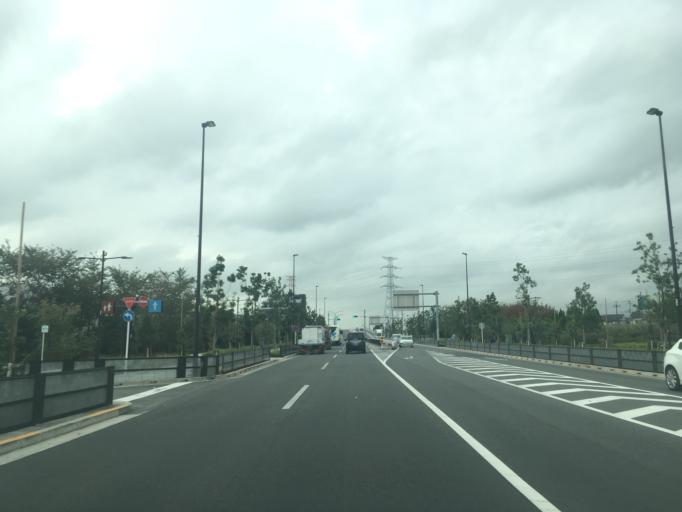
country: JP
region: Tokyo
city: Kokubunji
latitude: 35.7037
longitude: 139.4608
